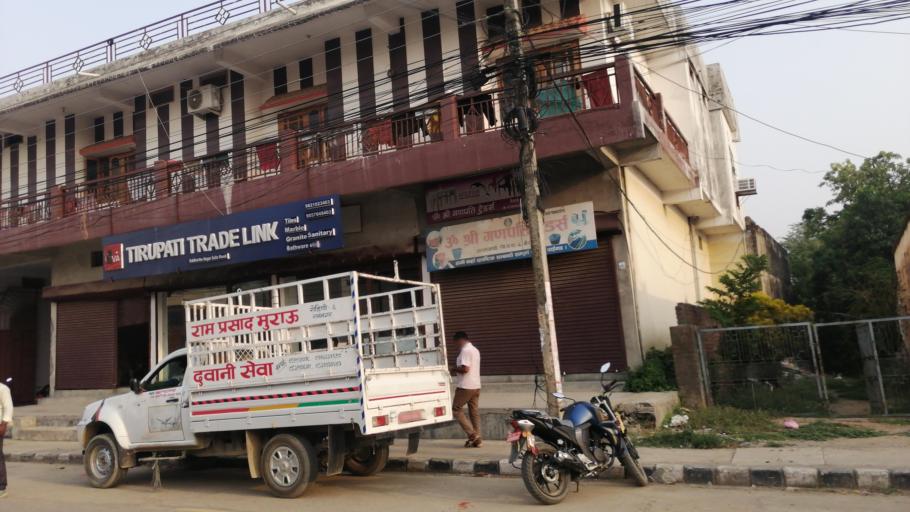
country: NP
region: Western Region
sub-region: Lumbini Zone
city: Bhairahawa
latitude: 27.5073
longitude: 83.4423
